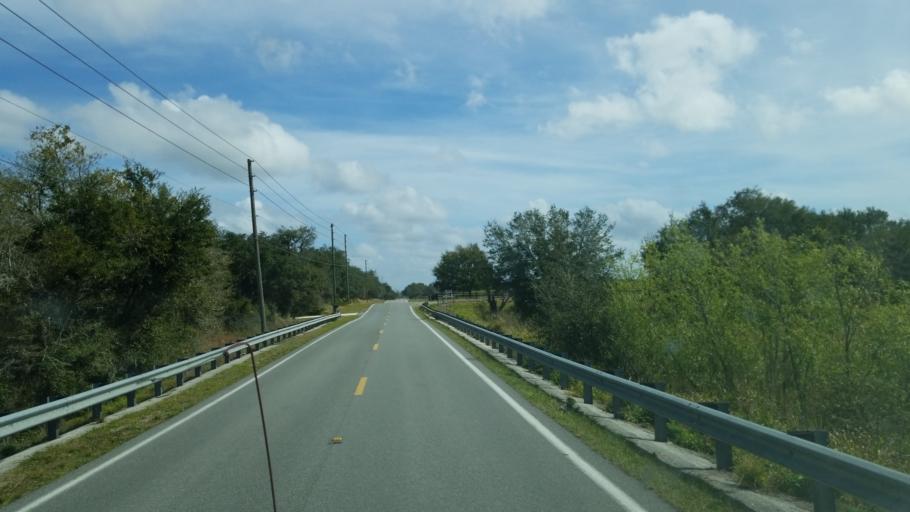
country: US
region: Florida
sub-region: Polk County
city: Lake Wales
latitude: 27.9252
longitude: -81.5141
